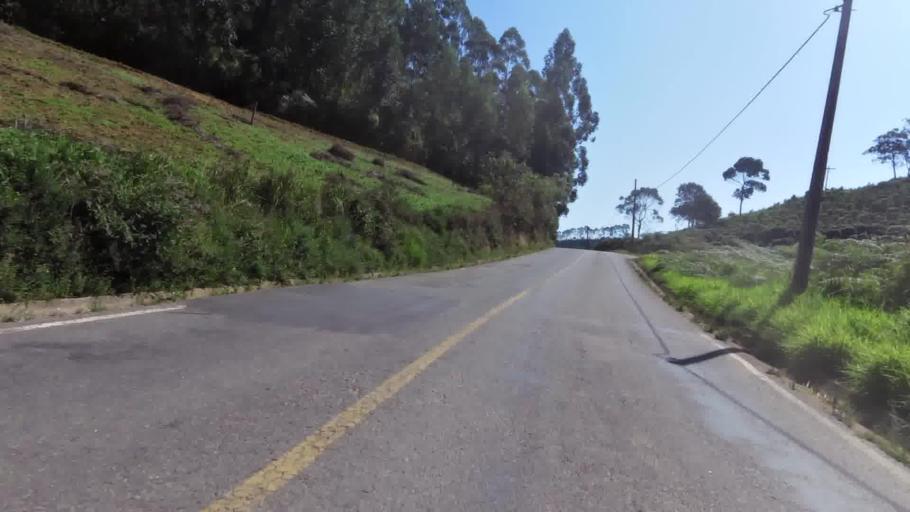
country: BR
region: Espirito Santo
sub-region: Marechal Floriano
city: Marechal Floriano
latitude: -20.4245
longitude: -40.8750
